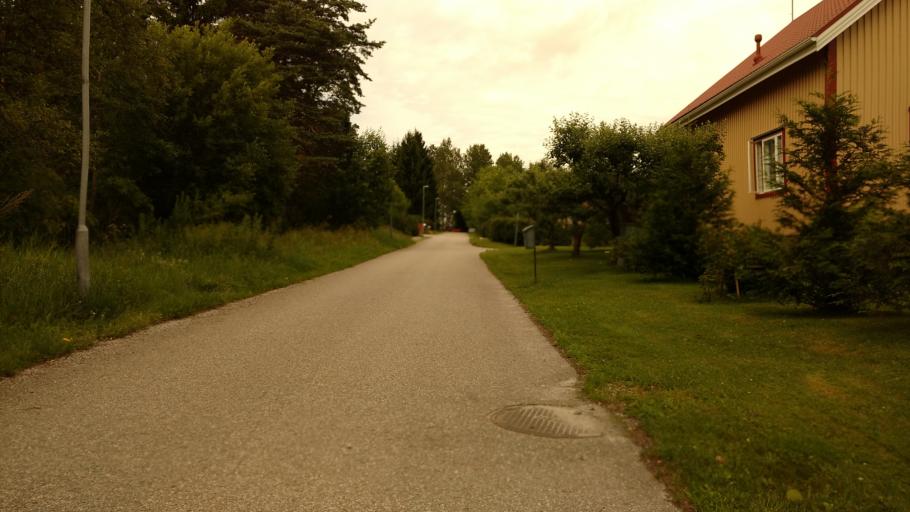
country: FI
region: Varsinais-Suomi
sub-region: Salo
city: Salo
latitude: 60.3925
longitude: 23.1666
